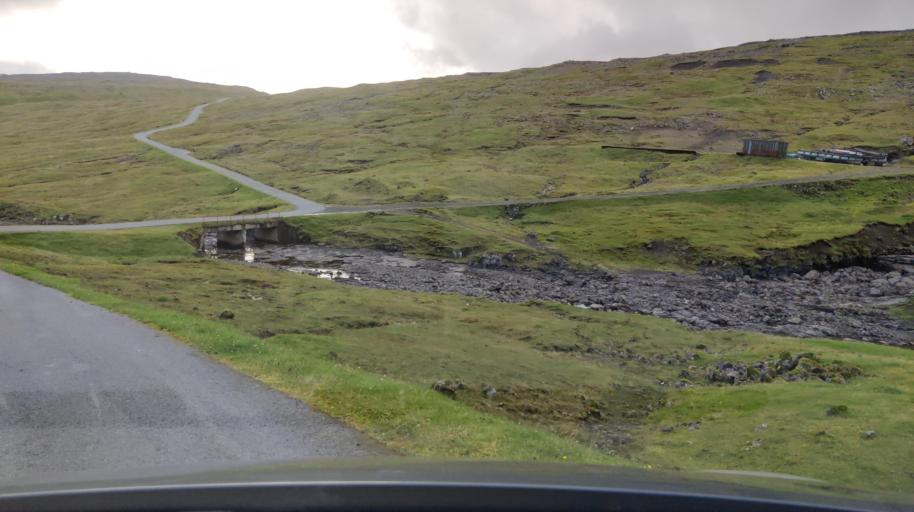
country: FO
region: Streymoy
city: Vestmanna
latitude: 62.1766
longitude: -7.1536
